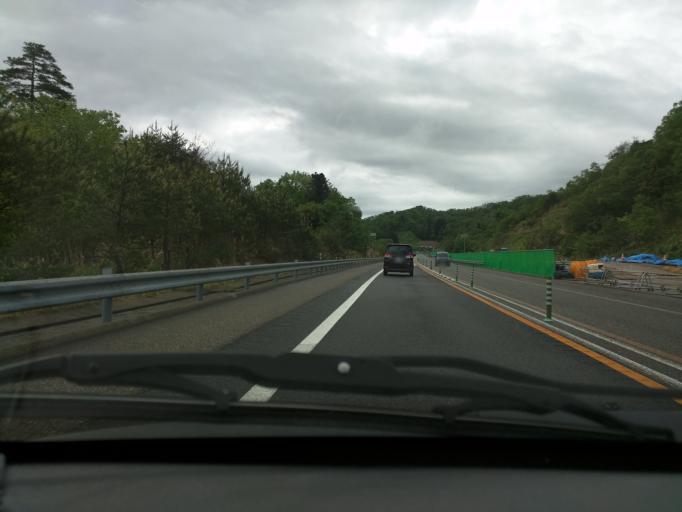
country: JP
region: Niigata
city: Joetsu
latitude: 37.1131
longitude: 138.2187
